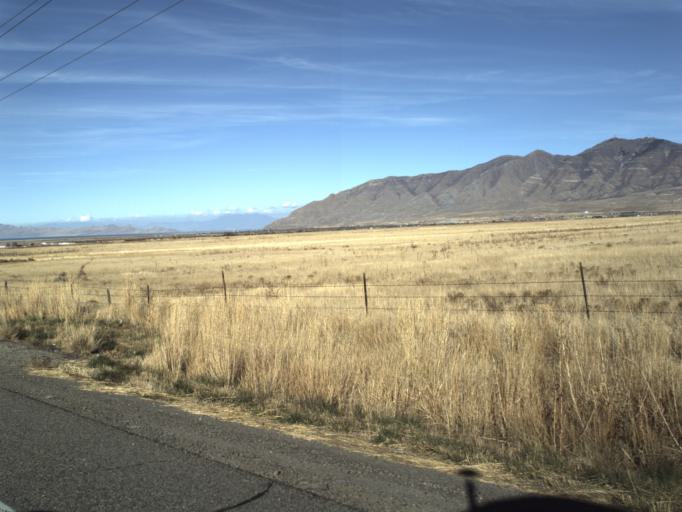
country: US
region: Utah
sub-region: Tooele County
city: Erda
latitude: 40.5679
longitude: -112.3672
